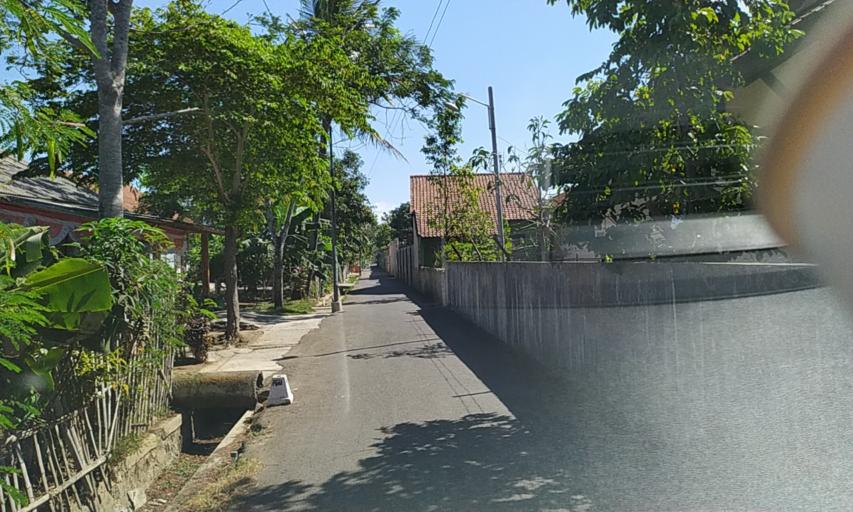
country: ID
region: Central Java
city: Rejanegara
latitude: -7.6854
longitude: 109.0387
